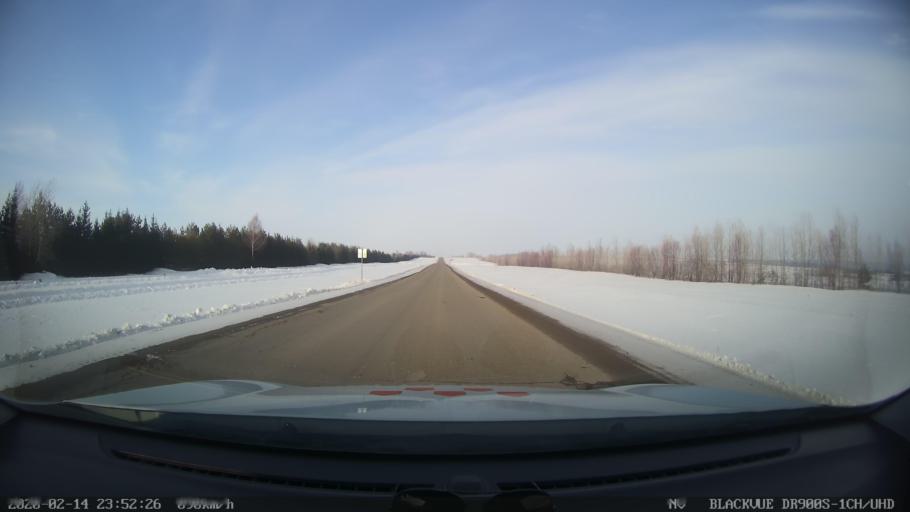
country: RU
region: Tatarstan
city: Kuybyshevskiy Zaton
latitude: 55.2786
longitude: 49.1434
